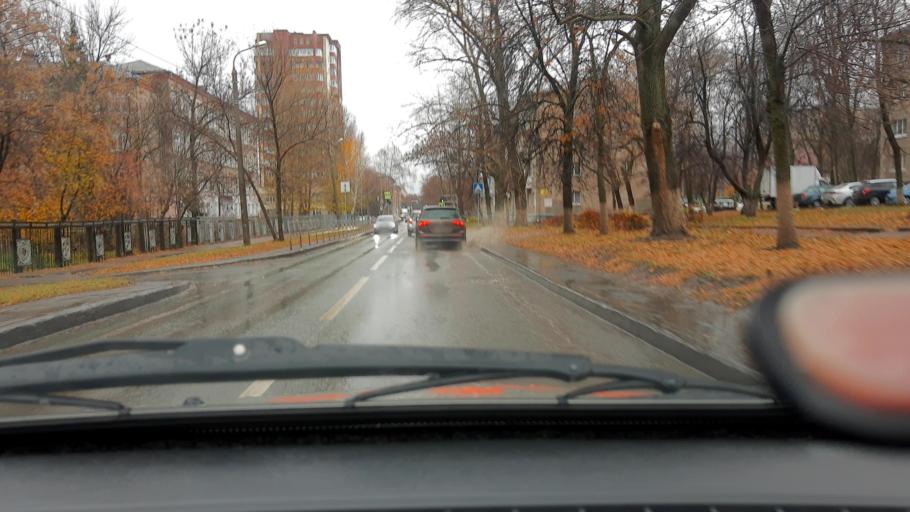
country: RU
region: Bashkortostan
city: Ufa
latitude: 54.7872
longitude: 56.0294
